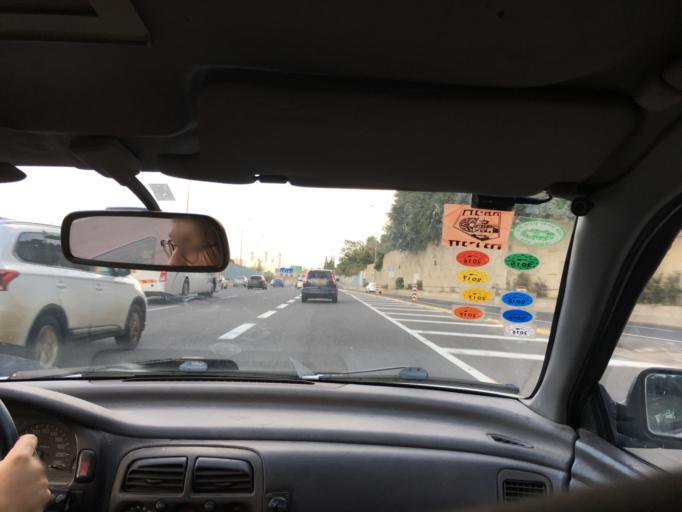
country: IL
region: Tel Aviv
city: Ramat Gan
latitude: 32.0912
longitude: 34.8013
